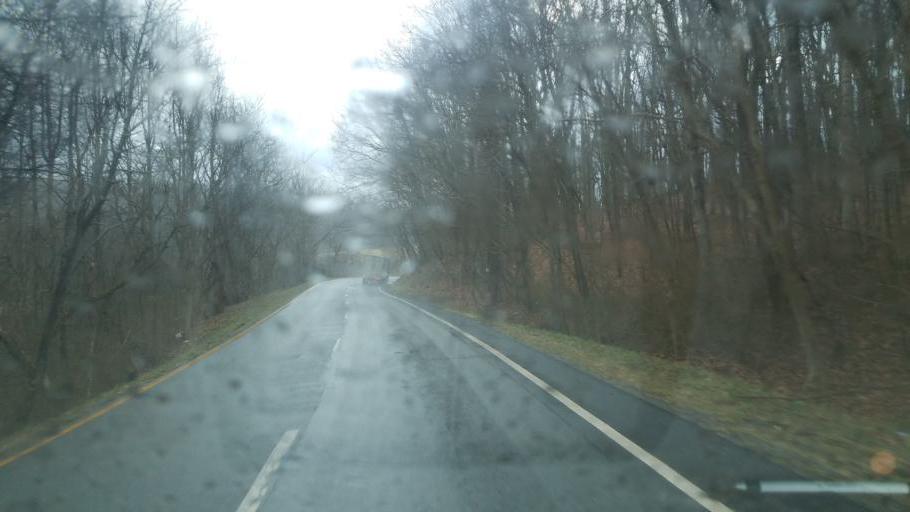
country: US
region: Virginia
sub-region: Giles County
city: Pearisburg
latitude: 37.2894
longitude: -80.7426
